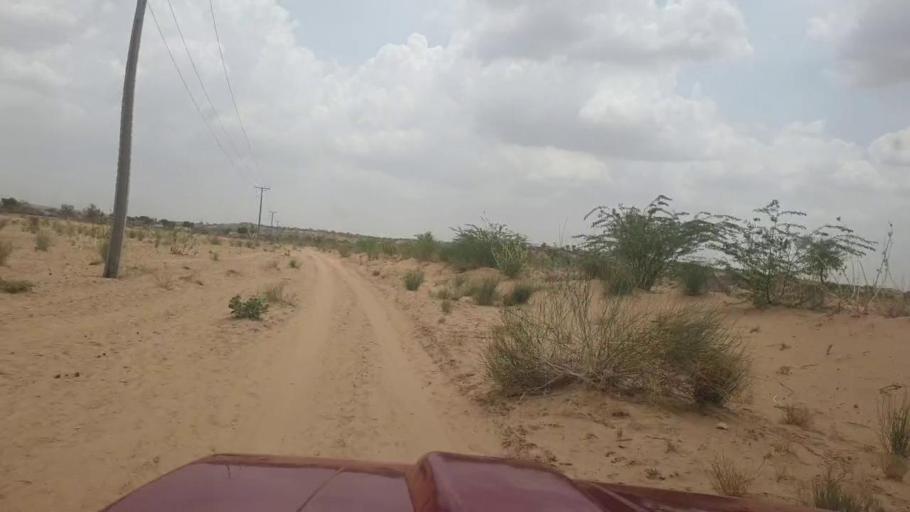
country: PK
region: Sindh
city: Islamkot
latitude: 25.1074
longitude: 70.3715
